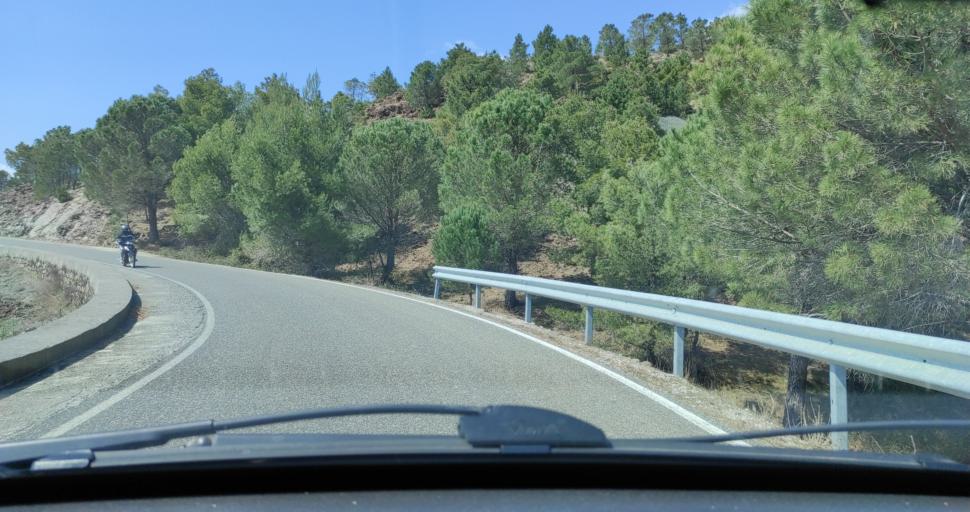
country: AL
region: Shkoder
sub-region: Rrethi i Shkodres
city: Hajmel
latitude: 41.9823
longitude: 19.6463
